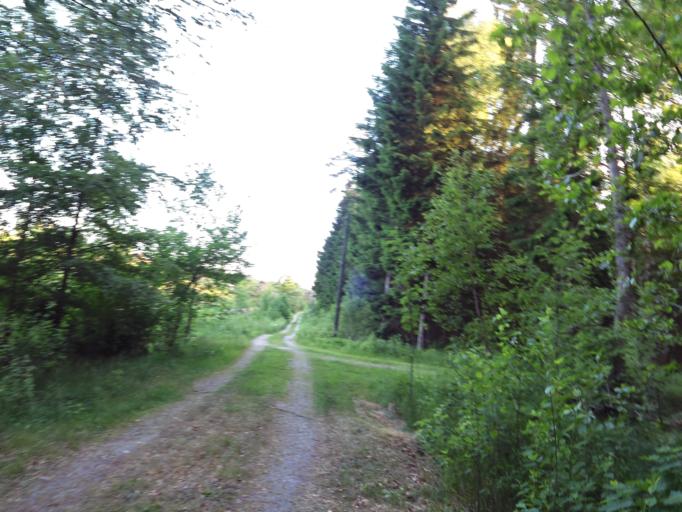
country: SE
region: Blekinge
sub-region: Olofstroms Kommun
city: Olofstroem
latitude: 56.4157
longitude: 14.5473
